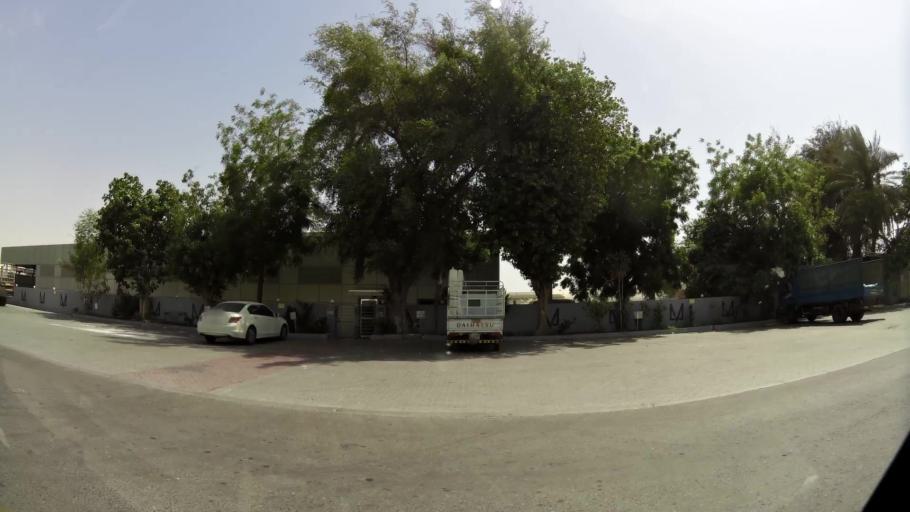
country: AE
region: Dubai
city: Dubai
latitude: 25.1507
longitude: 55.2368
